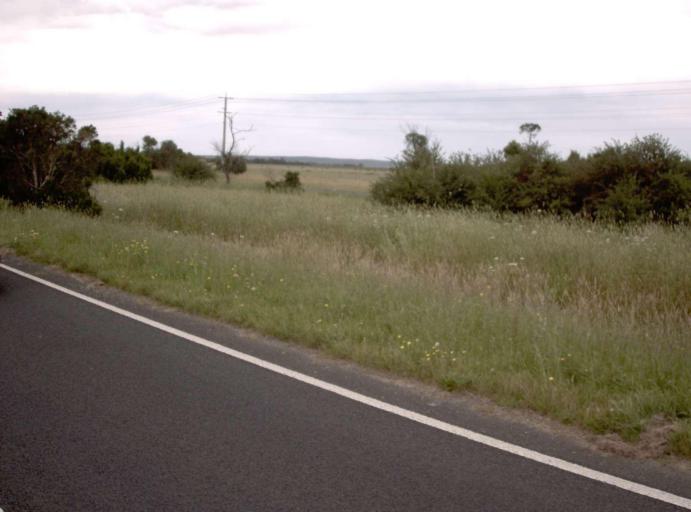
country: AU
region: Victoria
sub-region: Cardinia
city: Koo-Wee-Rup
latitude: -38.2608
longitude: 145.5503
